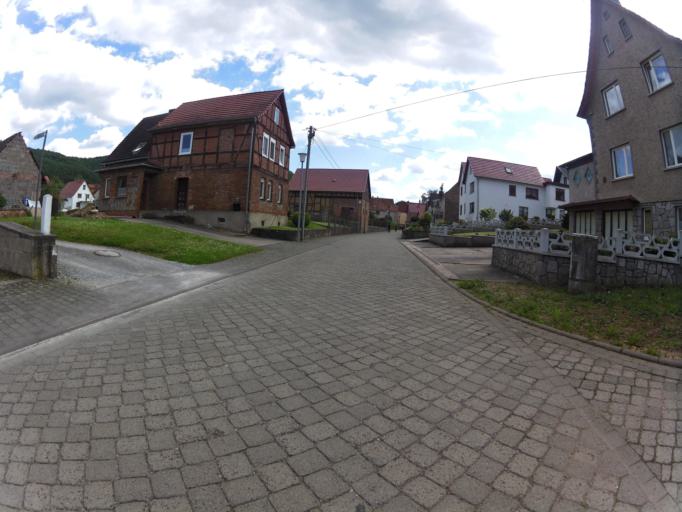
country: DE
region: Thuringia
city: Treffurt
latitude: 51.1082
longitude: 10.2195
